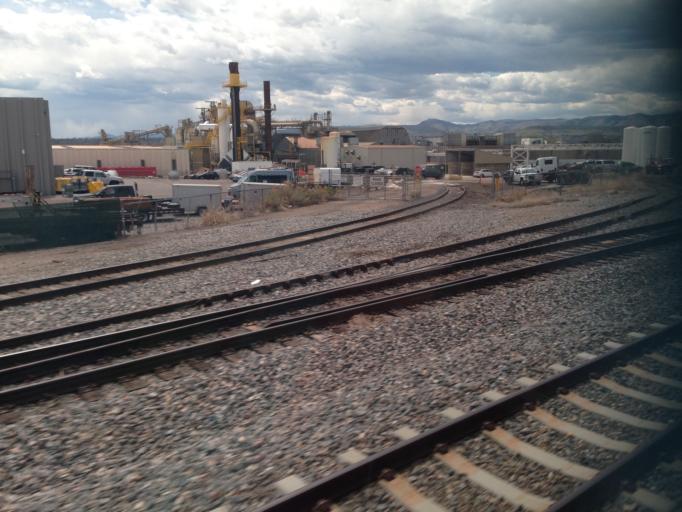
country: US
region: Colorado
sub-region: Jefferson County
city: Arvada
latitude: 39.7918
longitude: -105.1153
